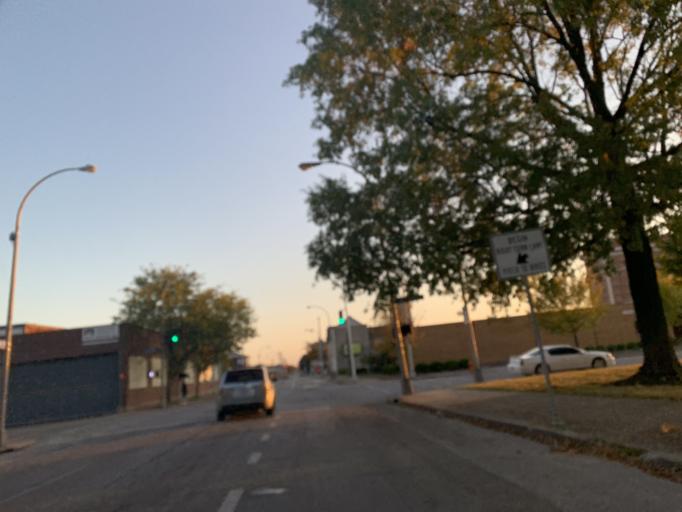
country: US
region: Kentucky
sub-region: Jefferson County
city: Louisville
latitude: 38.2487
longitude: -85.7647
